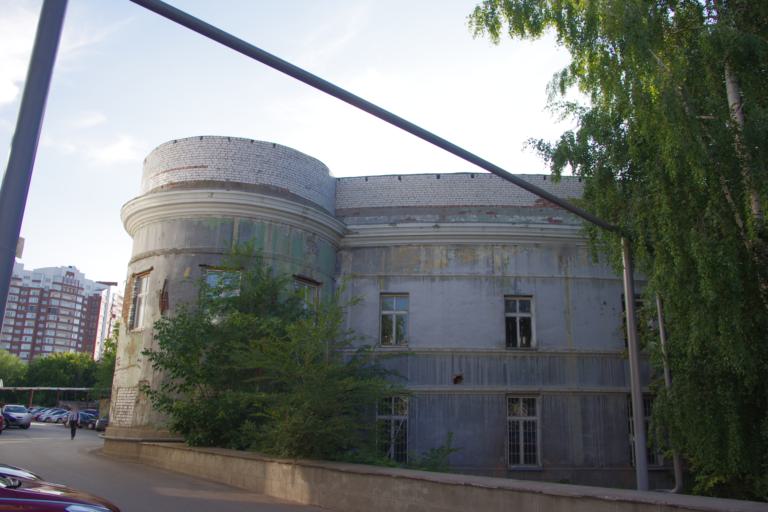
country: RU
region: Samara
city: Samara
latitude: 53.2156
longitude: 50.1498
